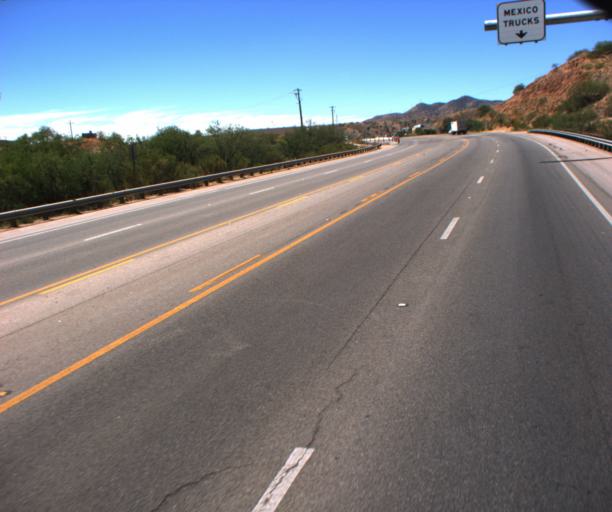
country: US
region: Arizona
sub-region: Santa Cruz County
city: Nogales
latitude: 31.3436
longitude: -110.9662
